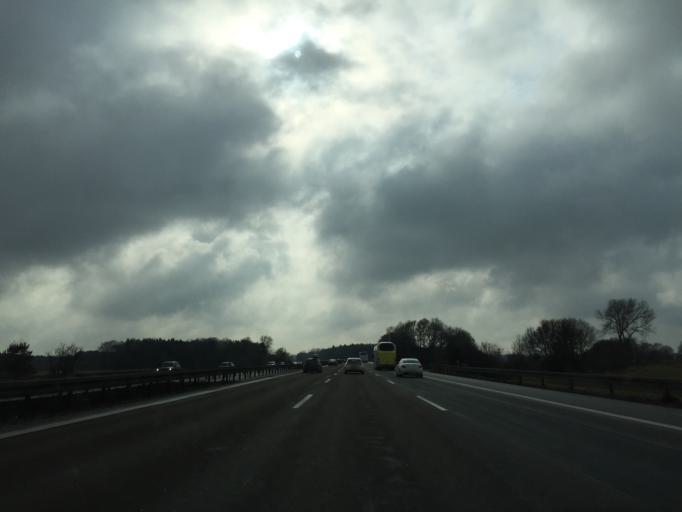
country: DE
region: Bavaria
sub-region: Upper Bavaria
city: Manching
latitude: 48.6989
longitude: 11.4897
